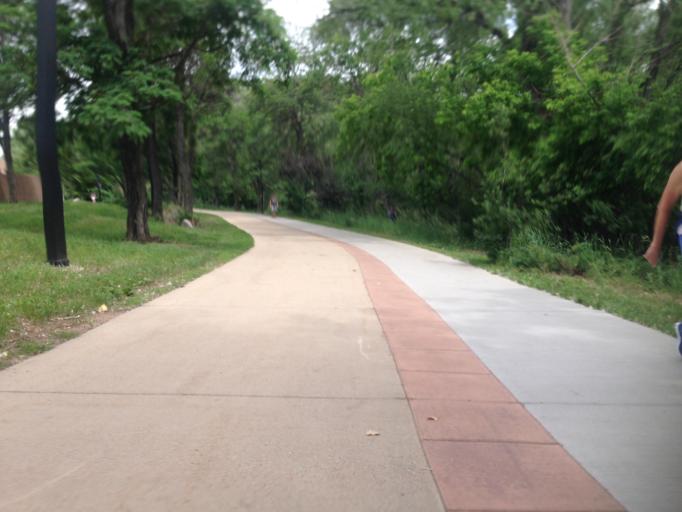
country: US
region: Colorado
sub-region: Boulder County
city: Boulder
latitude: 40.0139
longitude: -105.2903
